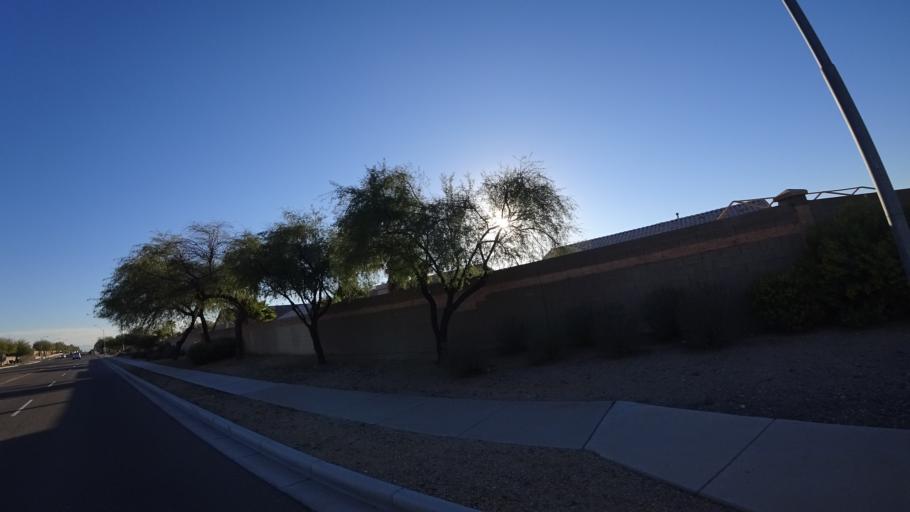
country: US
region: Arizona
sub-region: Maricopa County
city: Sun City West
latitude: 33.6765
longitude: -112.2900
